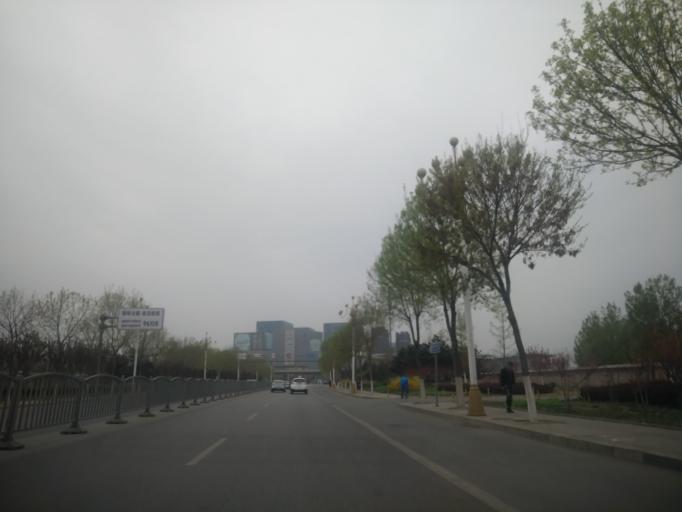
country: CN
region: Beijing
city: Jiugong
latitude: 39.8057
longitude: 116.4590
